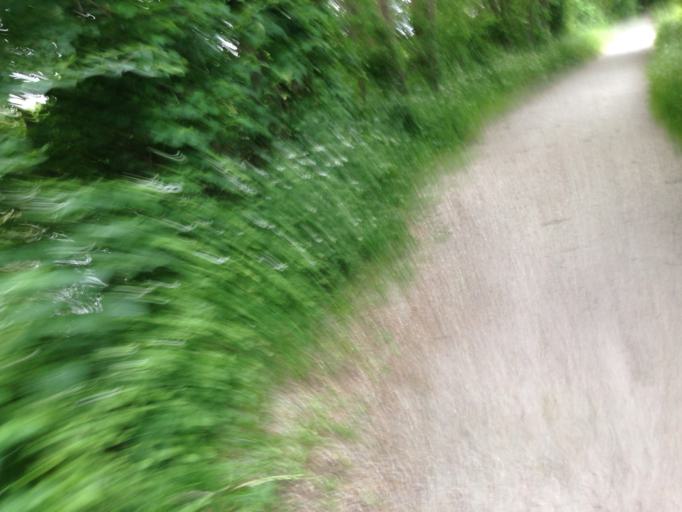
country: SE
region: Skane
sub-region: Lomma Kommun
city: Lomma
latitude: 55.6829
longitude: 13.0690
